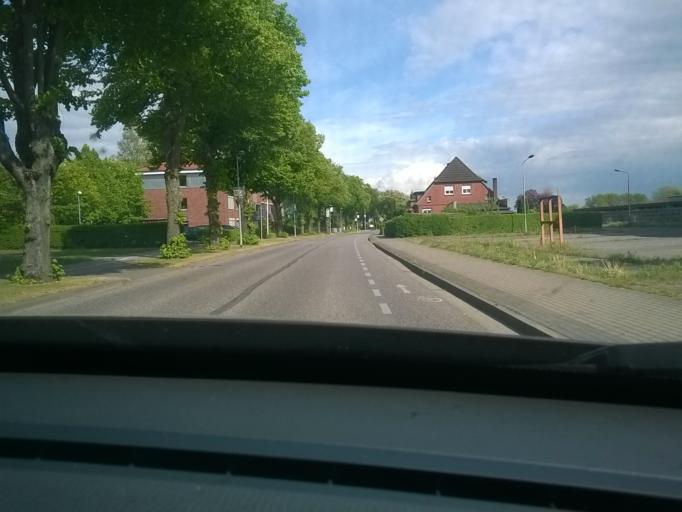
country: DE
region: Brandenburg
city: Wittstock
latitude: 53.1631
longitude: 12.4952
